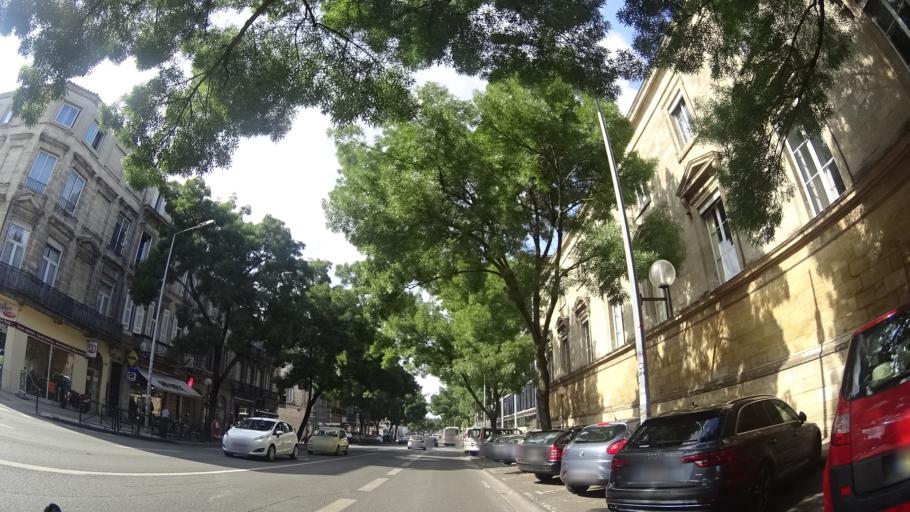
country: FR
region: Aquitaine
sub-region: Departement de la Gironde
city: Bordeaux
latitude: 44.8351
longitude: -0.5805
